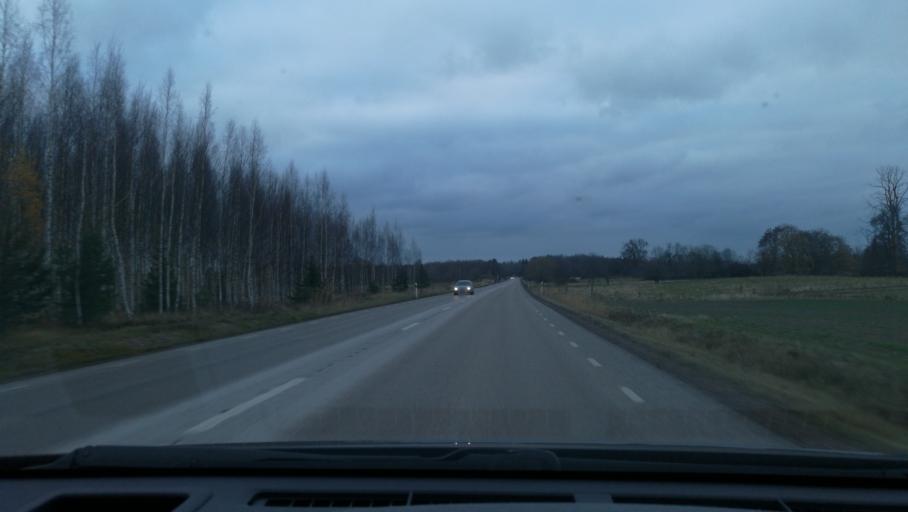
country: SE
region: Soedermanland
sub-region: Eskilstuna Kommun
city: Kvicksund
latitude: 59.4865
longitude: 16.3055
